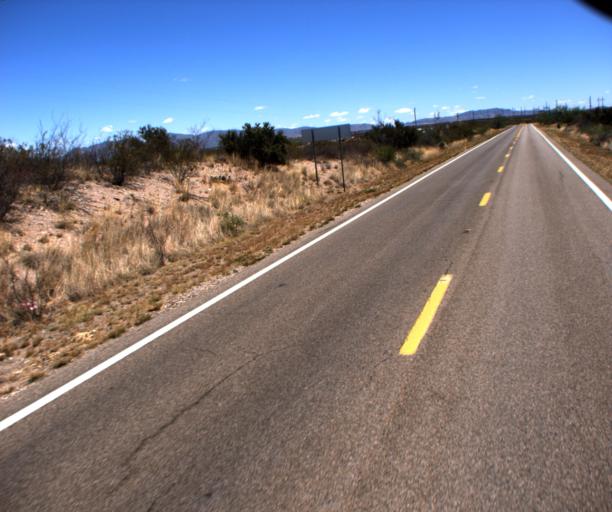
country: US
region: Arizona
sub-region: Cochise County
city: Tombstone
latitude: 31.7481
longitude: -110.1026
